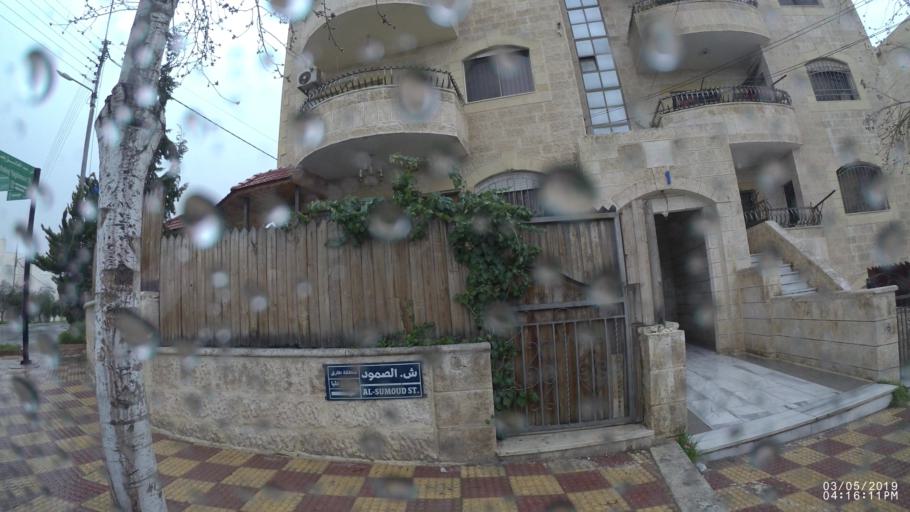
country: JO
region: Amman
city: Amman
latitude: 32.0034
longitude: 35.9542
